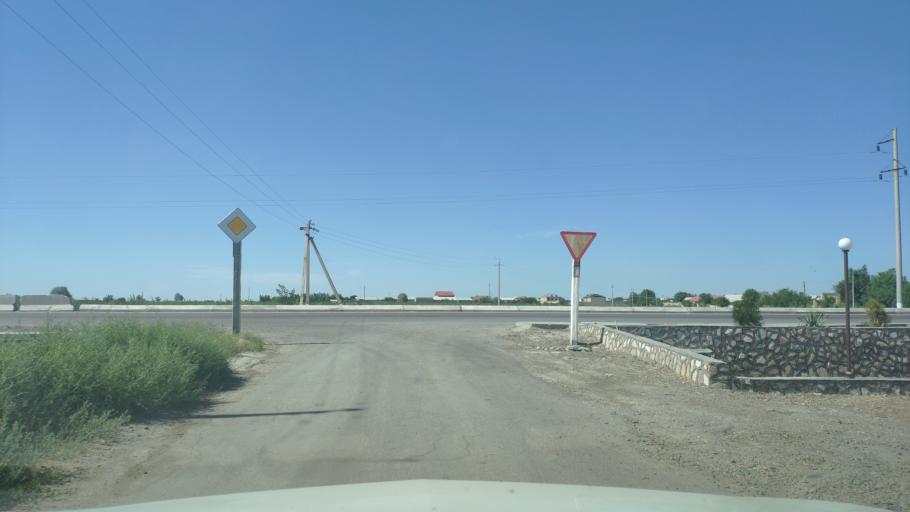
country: UZ
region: Bukhara
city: Bukhara
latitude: 39.7705
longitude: 64.3746
